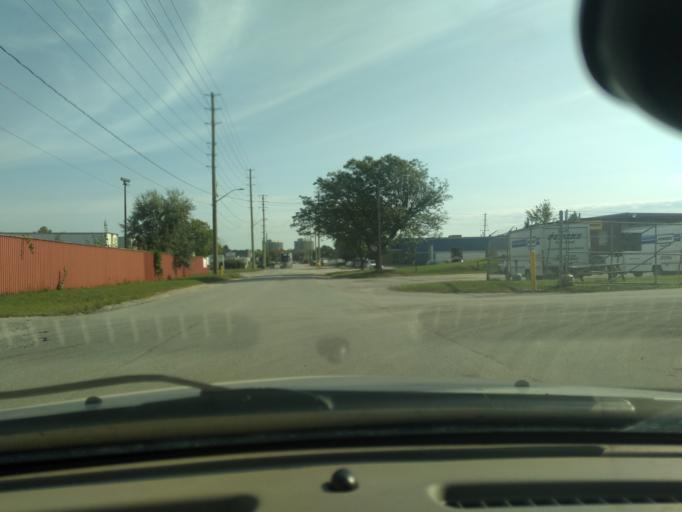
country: CA
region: Ontario
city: Barrie
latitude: 44.3756
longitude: -79.7057
